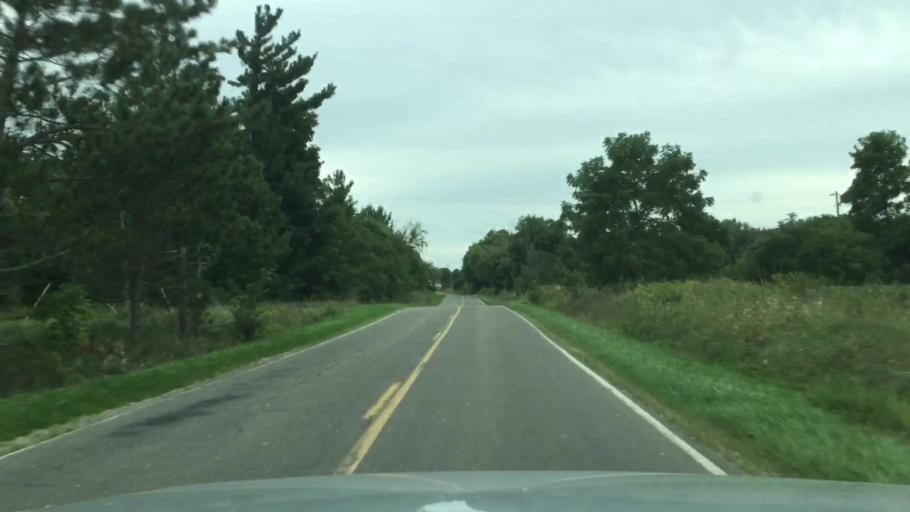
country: US
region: Michigan
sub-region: Shiawassee County
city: Durand
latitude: 42.8500
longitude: -84.0372
